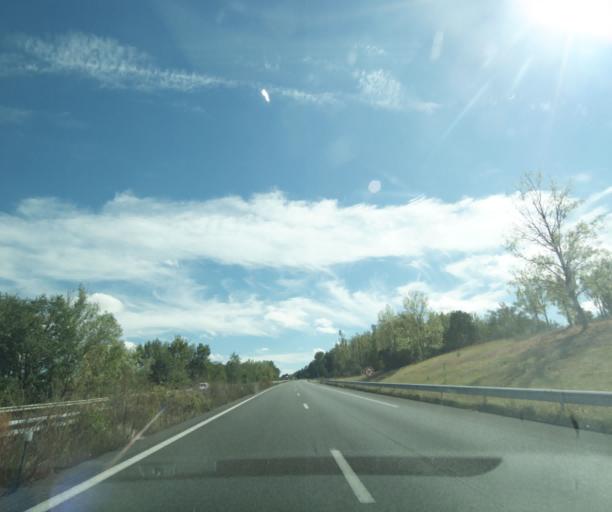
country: FR
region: Midi-Pyrenees
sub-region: Departement du Tarn-et-Garonne
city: Lamagistere
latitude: 44.0856
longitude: 0.7951
